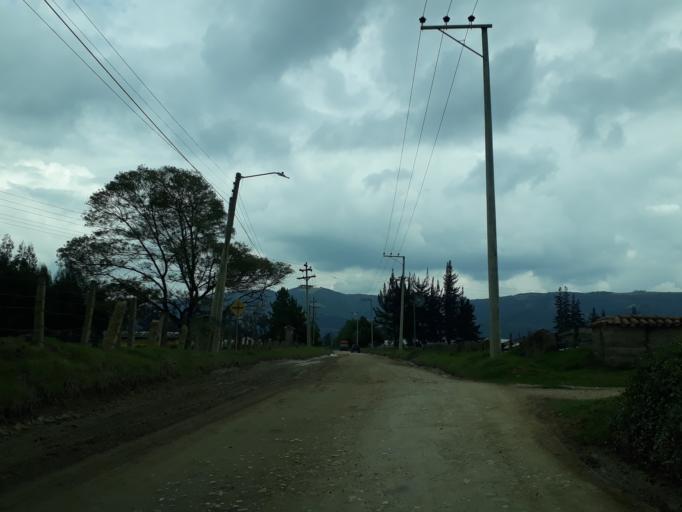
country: CO
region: Cundinamarca
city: Sesquile
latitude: 5.0654
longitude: -73.8080
